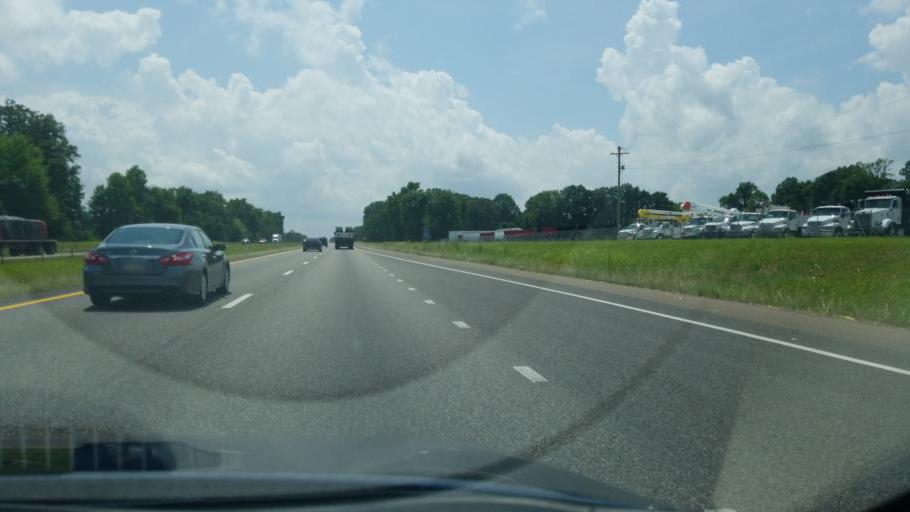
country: US
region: Tennessee
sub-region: Madison County
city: Jackson
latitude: 35.6319
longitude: -88.9531
